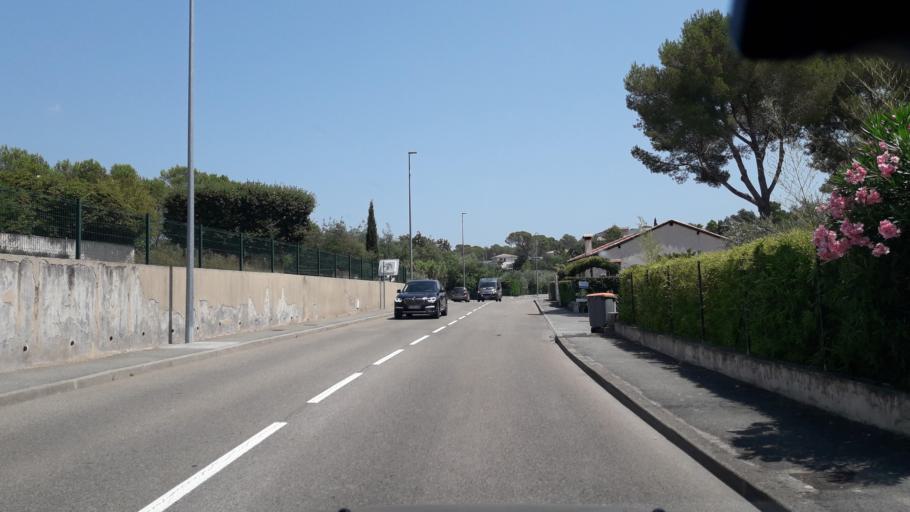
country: FR
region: Provence-Alpes-Cote d'Azur
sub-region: Departement du Var
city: Saint-Raphael
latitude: 43.4400
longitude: 6.7863
